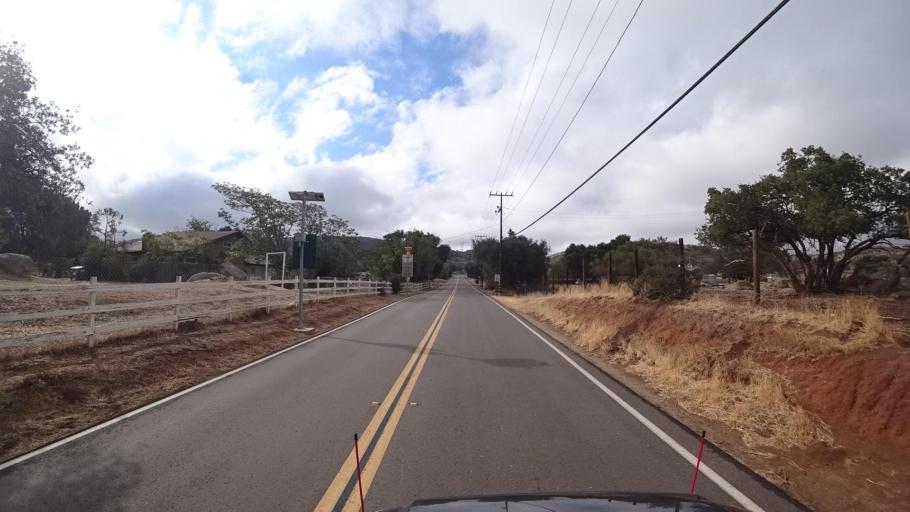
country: MX
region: Baja California
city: Tecate
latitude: 32.6086
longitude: -116.6132
